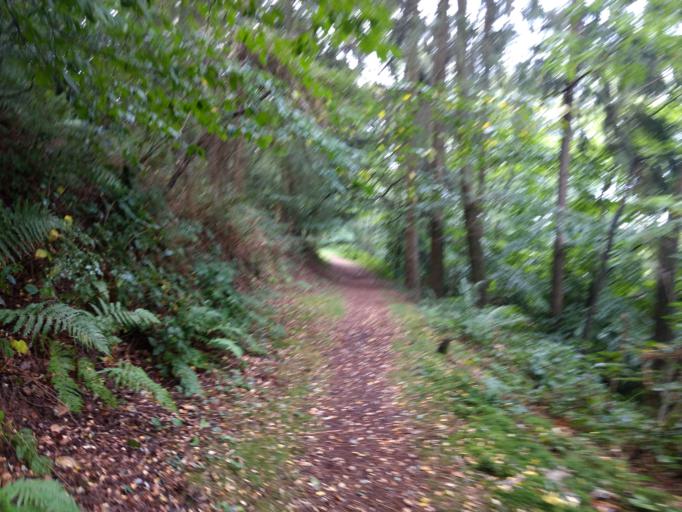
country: DE
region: Saarland
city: Nalbach
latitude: 49.3965
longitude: 6.8033
